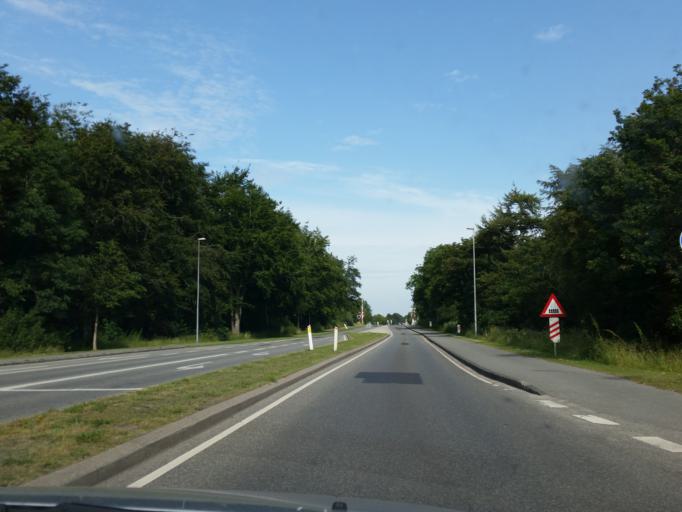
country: DK
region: South Denmark
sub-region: Tonder Kommune
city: Tonder
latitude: 54.9458
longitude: 8.8555
